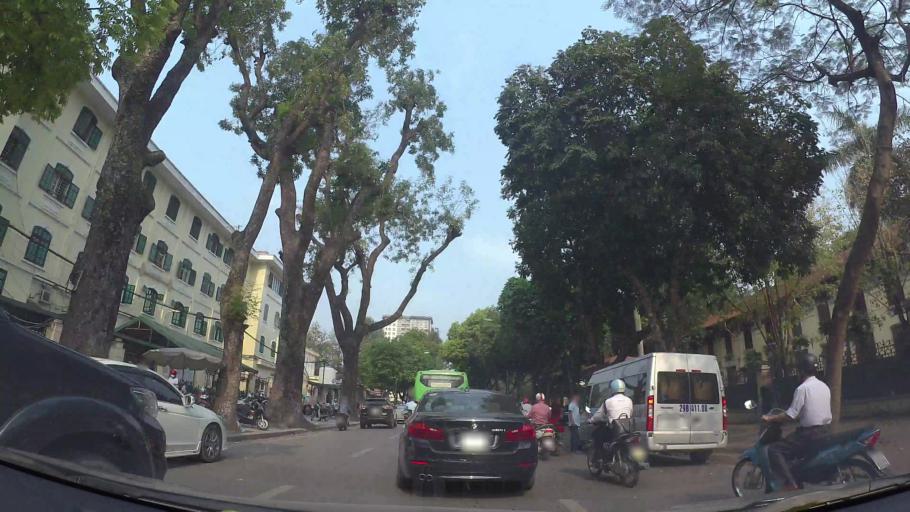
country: VN
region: Ha Noi
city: Hanoi
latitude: 21.0318
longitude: 105.8352
